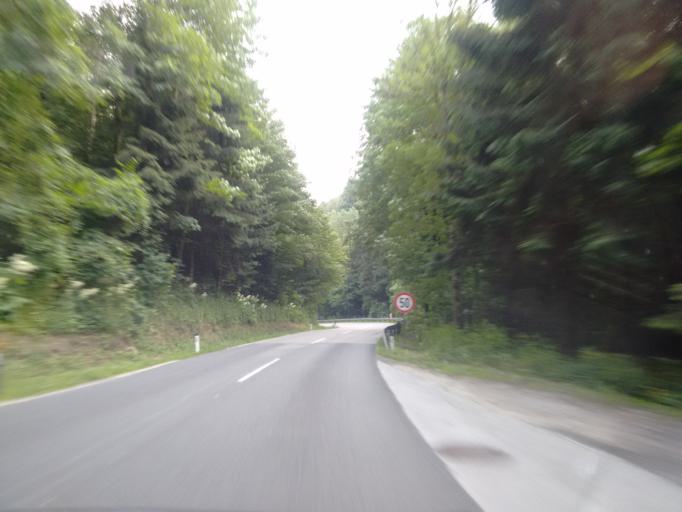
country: AT
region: Upper Austria
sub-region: Politischer Bezirk Urfahr-Umgebung
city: Altenberg bei Linz
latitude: 48.3592
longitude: 14.3338
